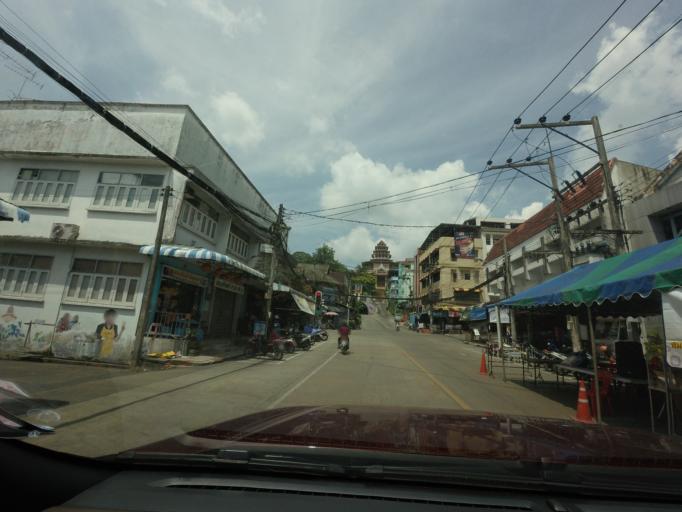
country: TH
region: Yala
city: Betong
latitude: 5.7715
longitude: 101.0715
